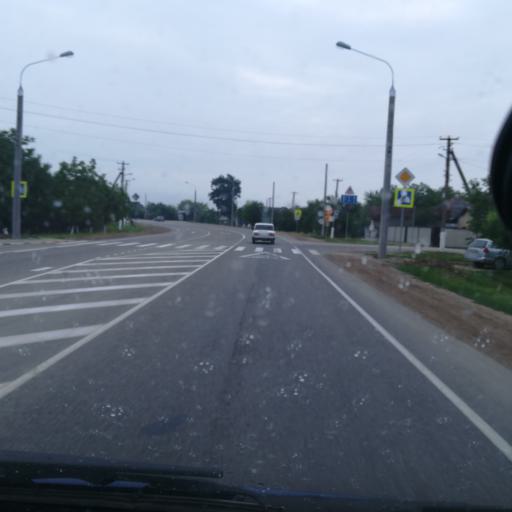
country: RU
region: Krasnodarskiy
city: Kiyevskoye
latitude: 44.9924
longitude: 37.9460
